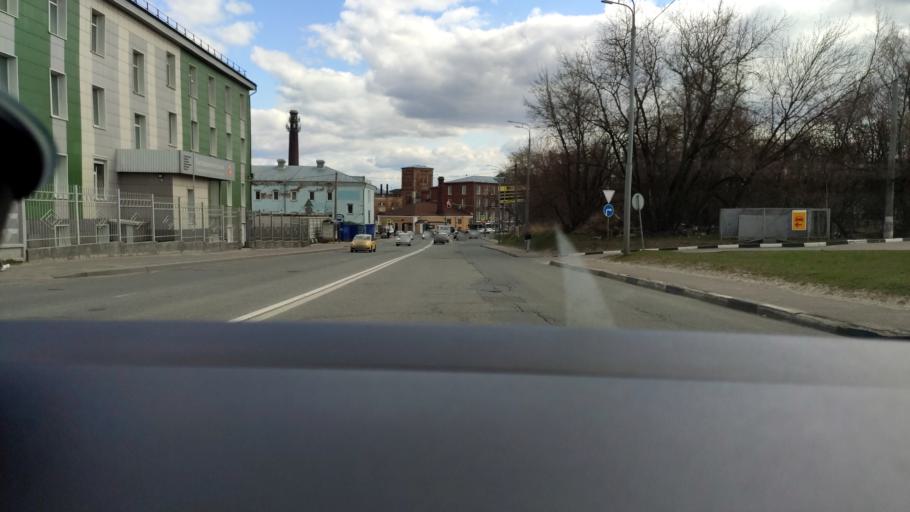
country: RU
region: Moskovskaya
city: Balashikha
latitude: 55.8158
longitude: 37.9532
